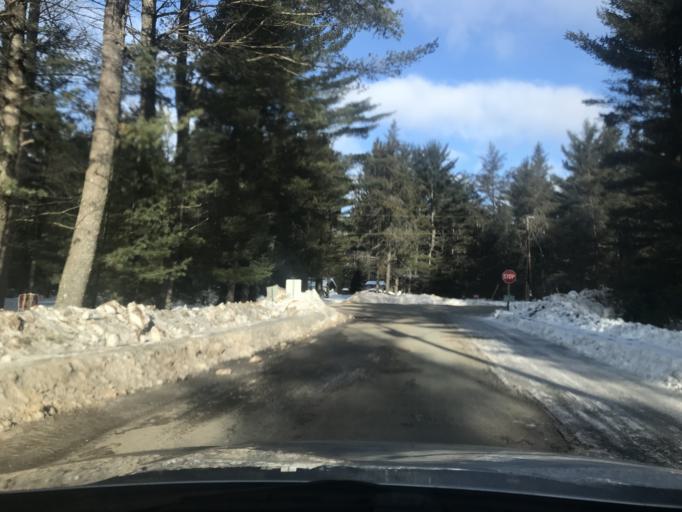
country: US
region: Wisconsin
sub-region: Marinette County
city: Niagara
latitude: 45.6373
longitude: -87.9705
